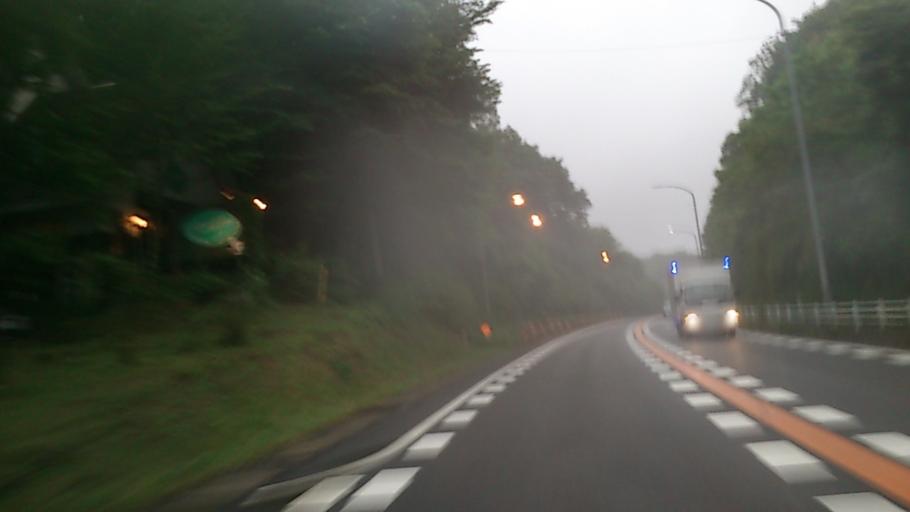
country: JP
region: Tochigi
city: Kuroiso
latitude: 37.0692
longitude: 140.1194
